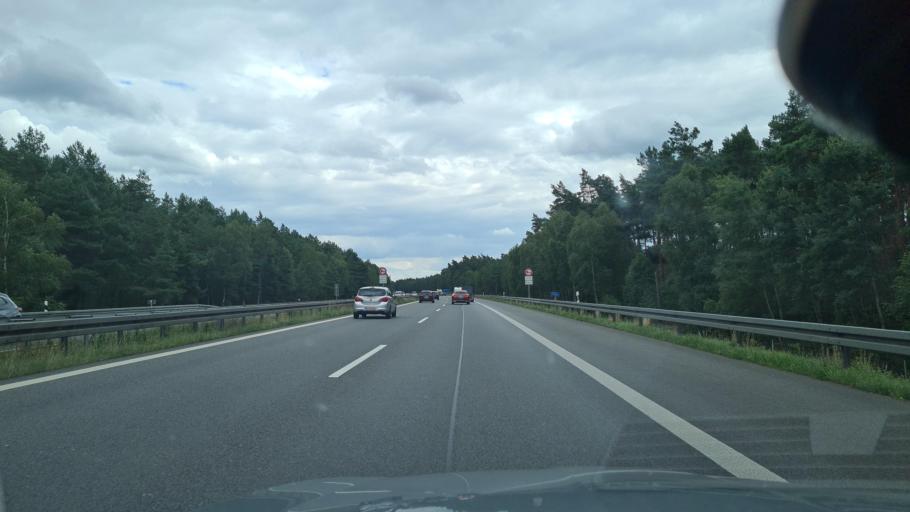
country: DE
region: Brandenburg
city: Wittstock
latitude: 53.1104
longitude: 12.4708
